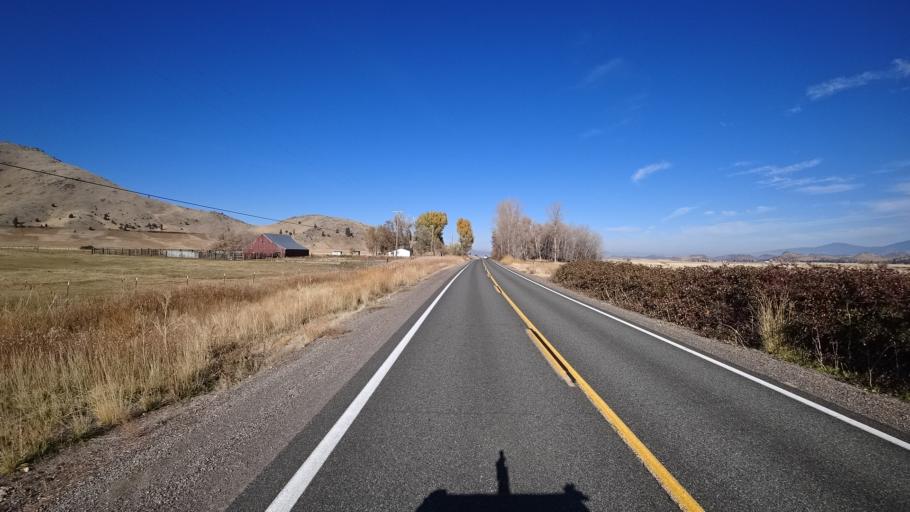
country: US
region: California
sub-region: Siskiyou County
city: Weed
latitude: 41.4575
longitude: -122.4610
